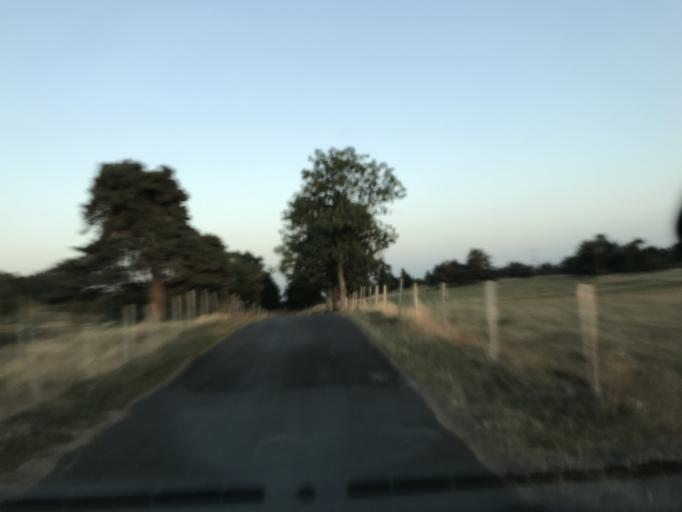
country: FR
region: Rhone-Alpes
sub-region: Departement de l'Ardeche
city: Saint-Agreve
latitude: 45.0264
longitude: 4.4365
